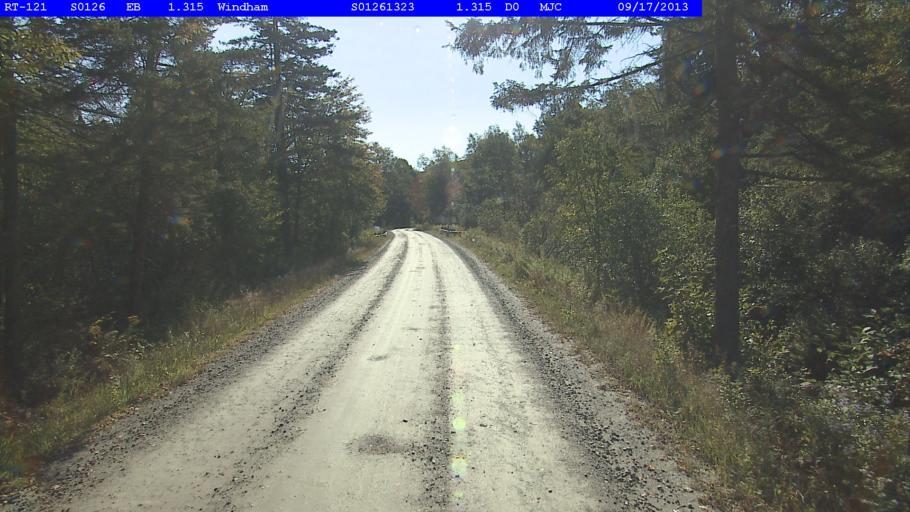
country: US
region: Vermont
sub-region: Windsor County
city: Chester
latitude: 43.1979
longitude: -72.6958
